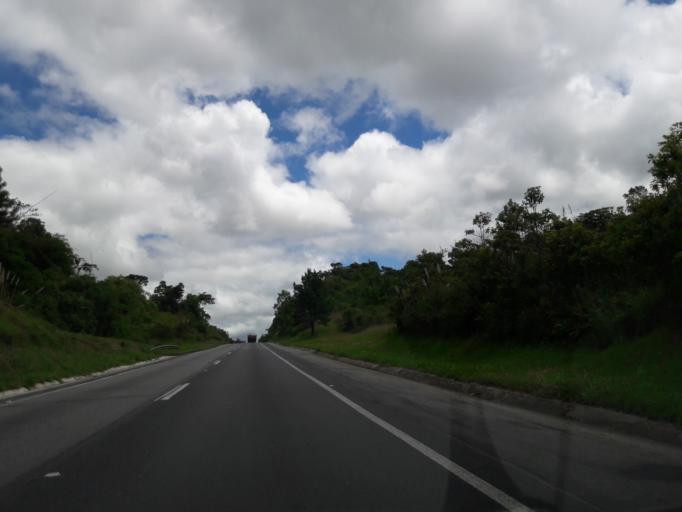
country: BR
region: Parana
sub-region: Antonina
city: Antonina
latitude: -25.1091
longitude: -48.7633
